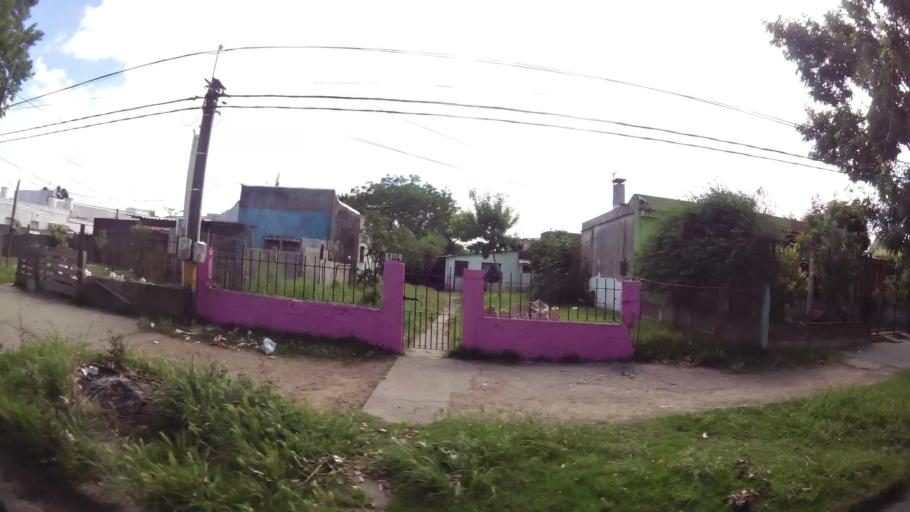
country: UY
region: Canelones
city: Paso de Carrasco
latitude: -34.8668
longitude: -56.1148
